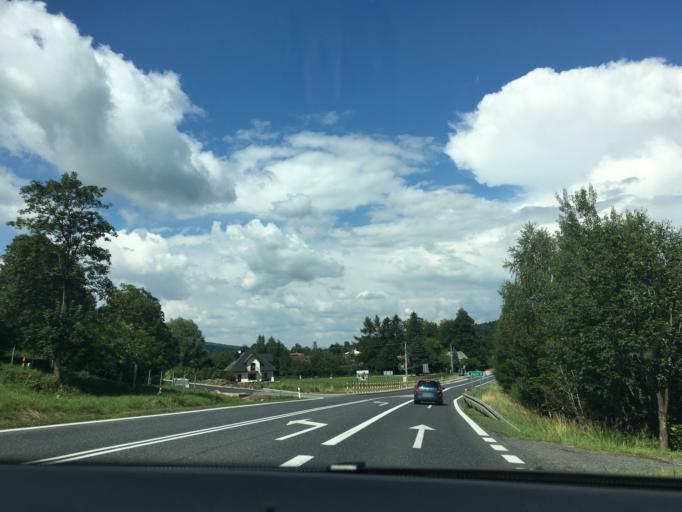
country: PL
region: Subcarpathian Voivodeship
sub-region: Powiat krosnienski
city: Dukla
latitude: 49.5696
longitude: 21.6943
